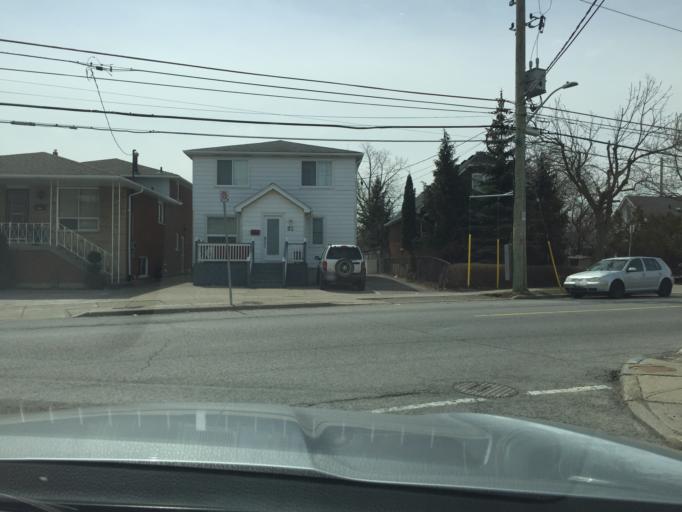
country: CA
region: Ontario
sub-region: Regional Municipality of Niagara
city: St. Catharines
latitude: 43.1770
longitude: -79.2225
